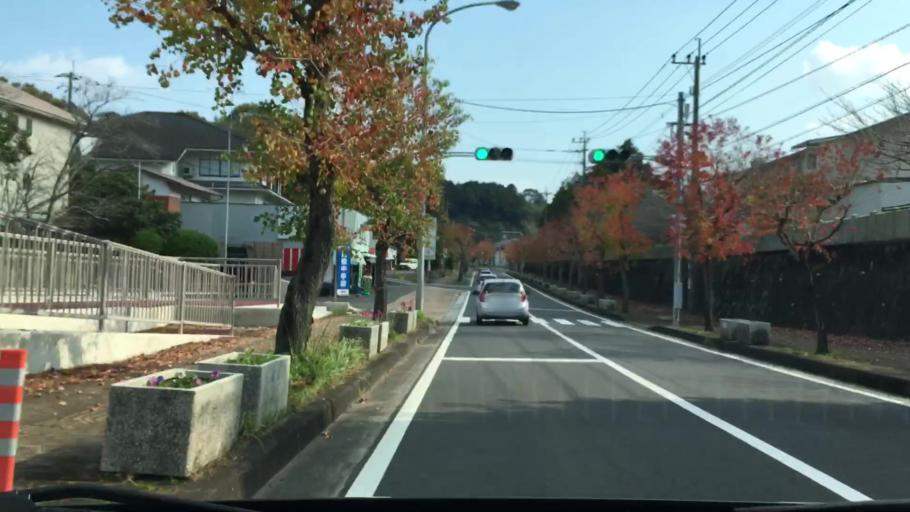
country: JP
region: Nagasaki
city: Sasebo
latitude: 32.9919
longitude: 129.7621
